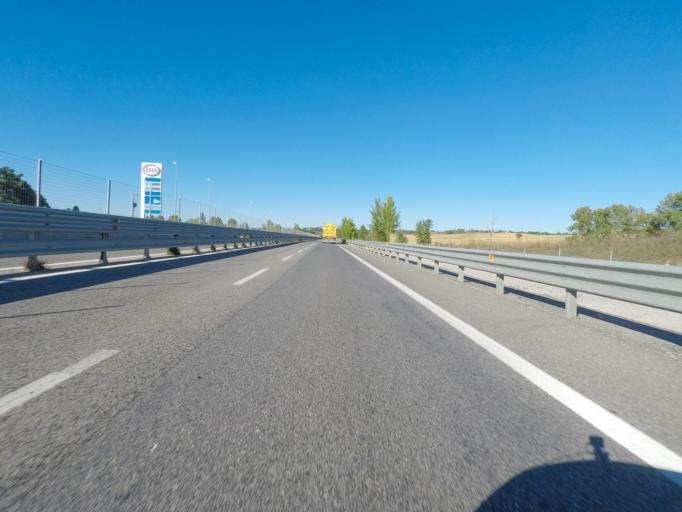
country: IT
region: Tuscany
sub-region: Provincia di Siena
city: Rosia
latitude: 43.2309
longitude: 11.2762
